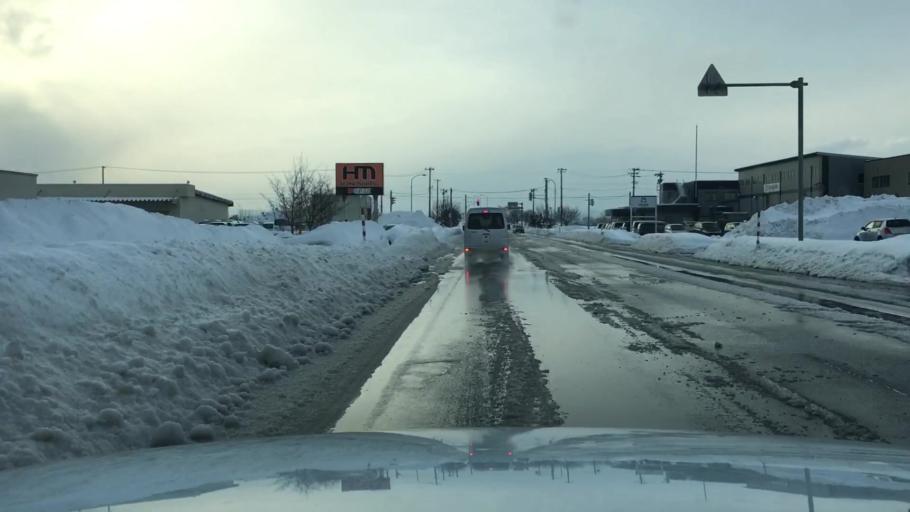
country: JP
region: Aomori
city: Hirosaki
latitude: 40.5944
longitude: 140.5328
